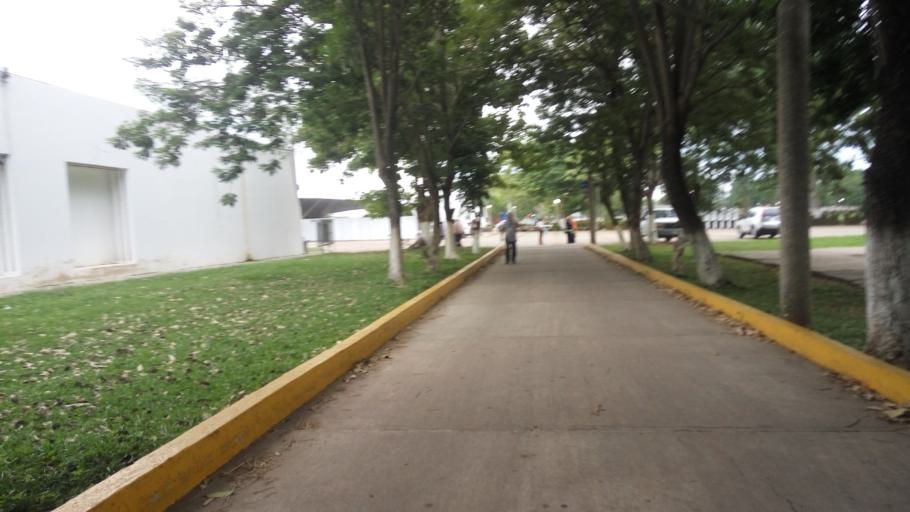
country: MX
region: Tabasco
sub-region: Nacajuca
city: Bosque de Saloya
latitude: 18.0074
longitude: -92.9627
